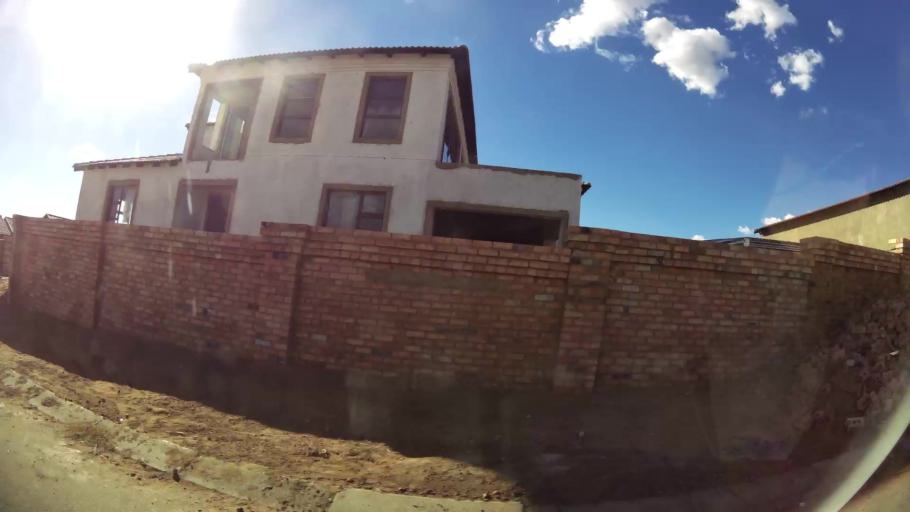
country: ZA
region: North-West
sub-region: Dr Kenneth Kaunda District Municipality
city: Klerksdorp
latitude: -26.8172
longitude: 26.6812
